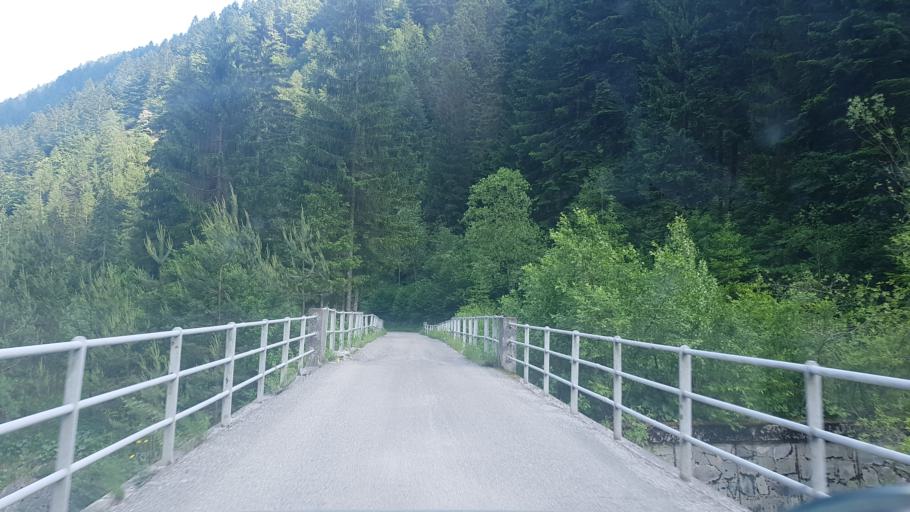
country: IT
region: Friuli Venezia Giulia
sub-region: Provincia di Udine
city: Pontebba
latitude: 46.5257
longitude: 13.2262
